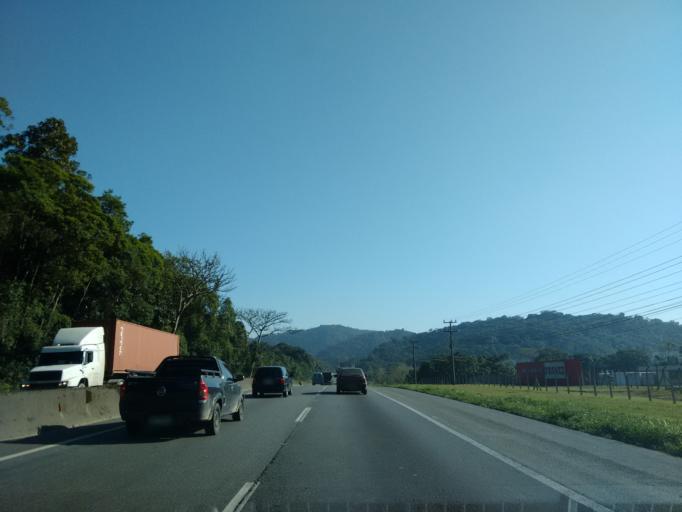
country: BR
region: Santa Catarina
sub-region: Joinville
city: Joinville
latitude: -26.2403
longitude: -48.9125
